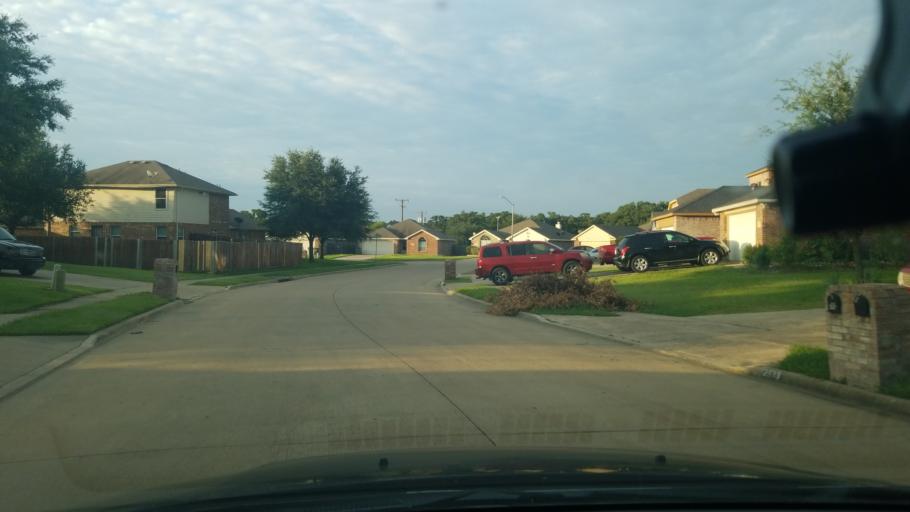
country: US
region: Texas
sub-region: Dallas County
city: Balch Springs
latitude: 32.7354
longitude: -96.6385
